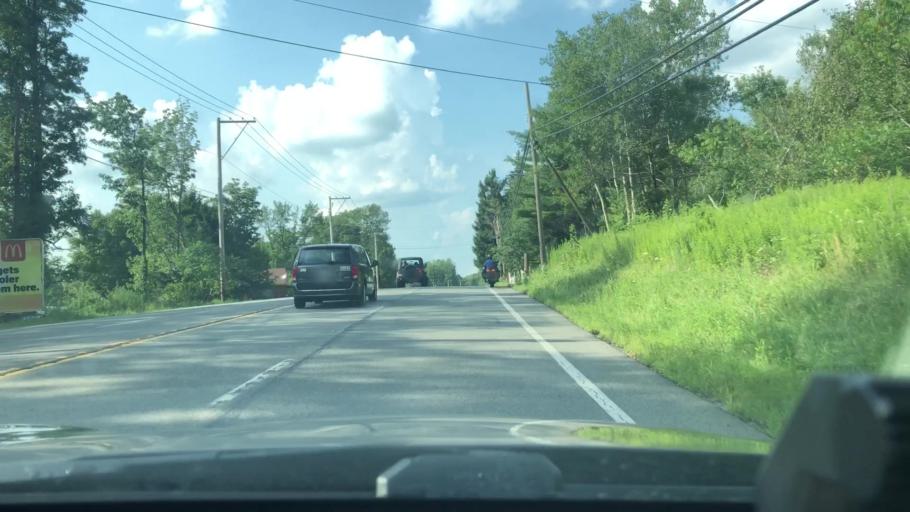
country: US
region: Pennsylvania
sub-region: Lackawanna County
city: Moscow
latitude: 41.2622
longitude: -75.5067
